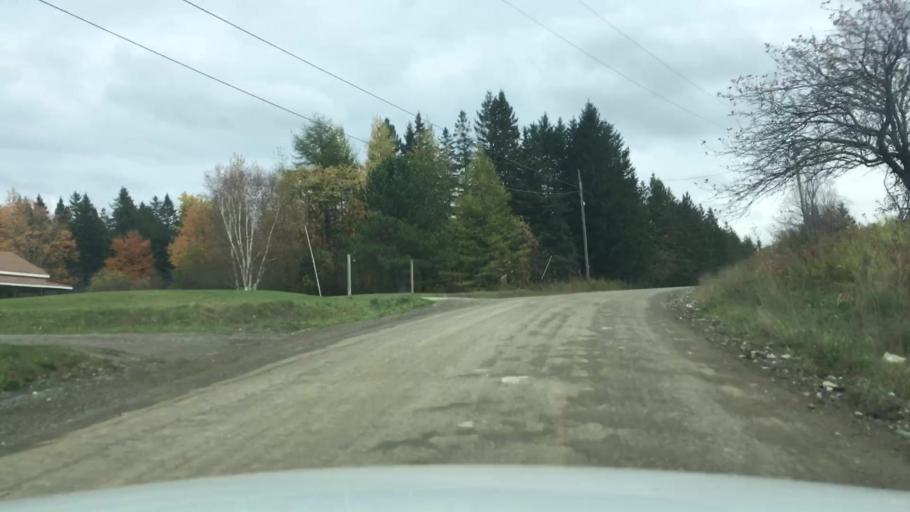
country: US
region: Maine
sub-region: Aroostook County
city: Easton
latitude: 46.5212
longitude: -67.8883
